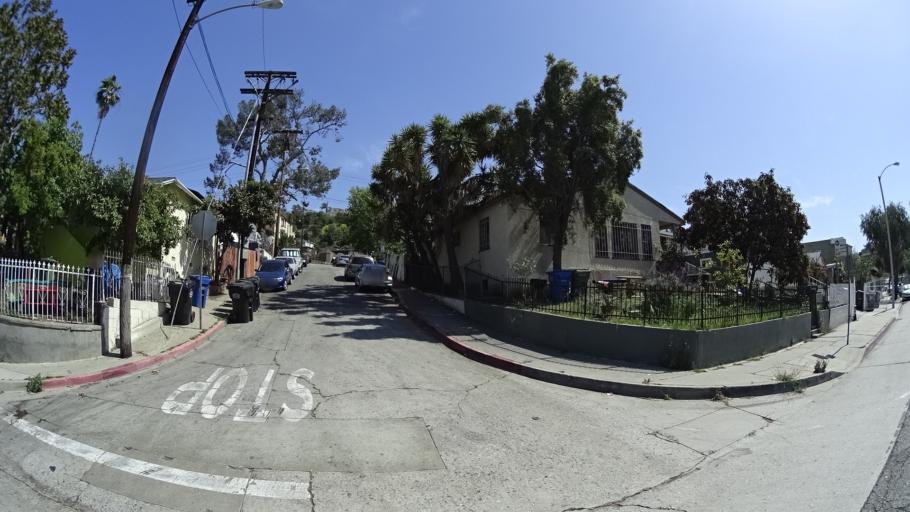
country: US
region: California
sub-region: Los Angeles County
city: Belvedere
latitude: 34.0544
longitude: -118.1875
